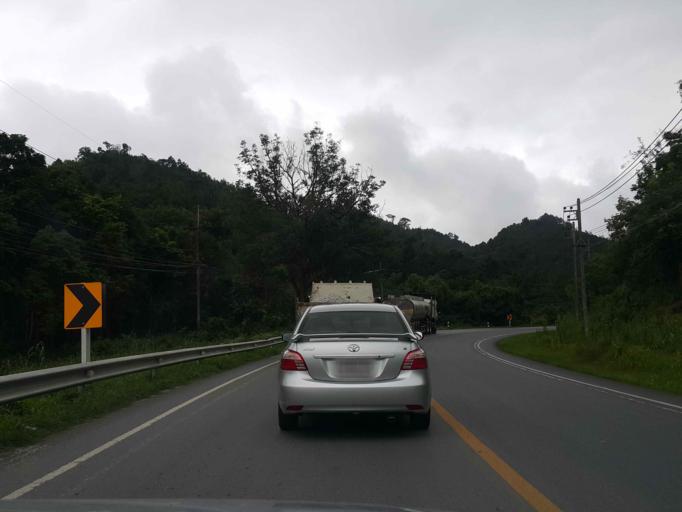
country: TH
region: Tak
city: Tak
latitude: 16.7883
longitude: 98.9453
